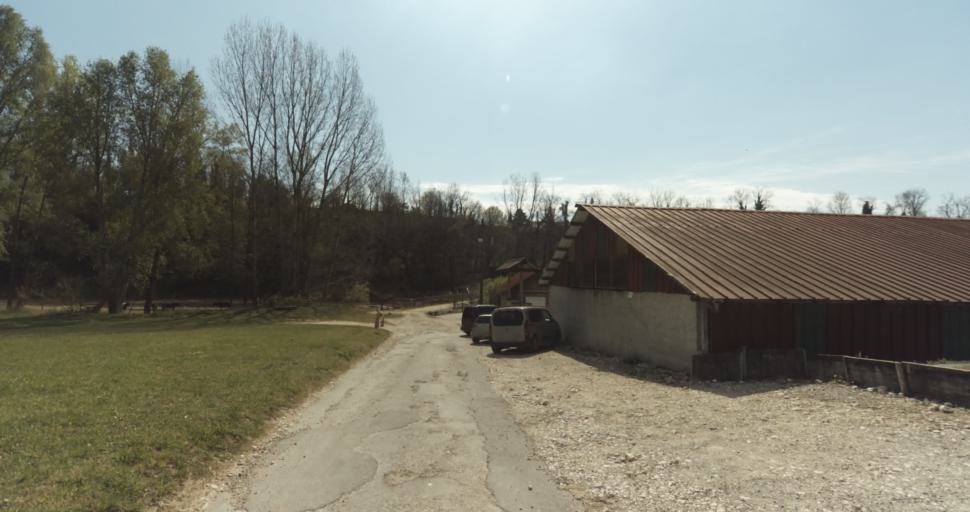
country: FR
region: Rhone-Alpes
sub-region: Departement de l'Isere
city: Saint-Verand
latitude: 45.1624
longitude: 5.3299
